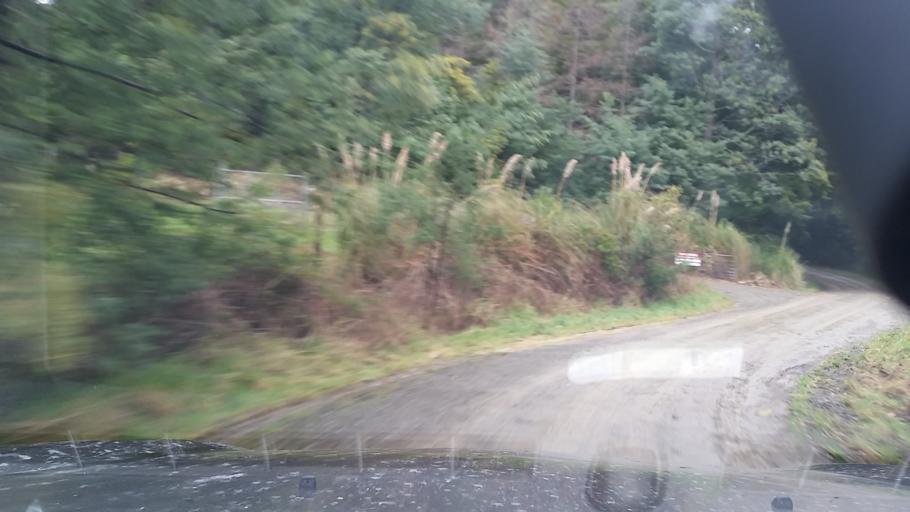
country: NZ
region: Nelson
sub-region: Nelson City
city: Nelson
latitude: -41.3741
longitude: 173.5985
